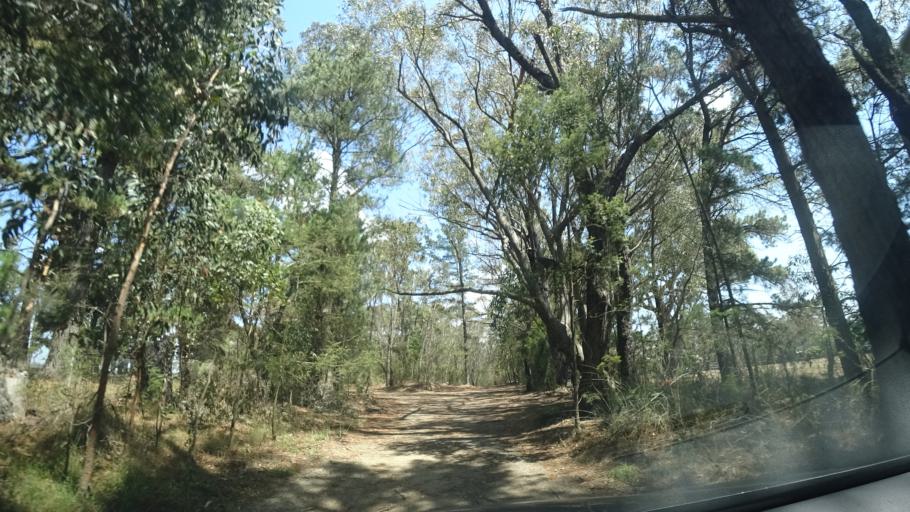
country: AU
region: New South Wales
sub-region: Wingecarribee
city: Bundanoon
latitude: -34.6361
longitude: 150.2547
